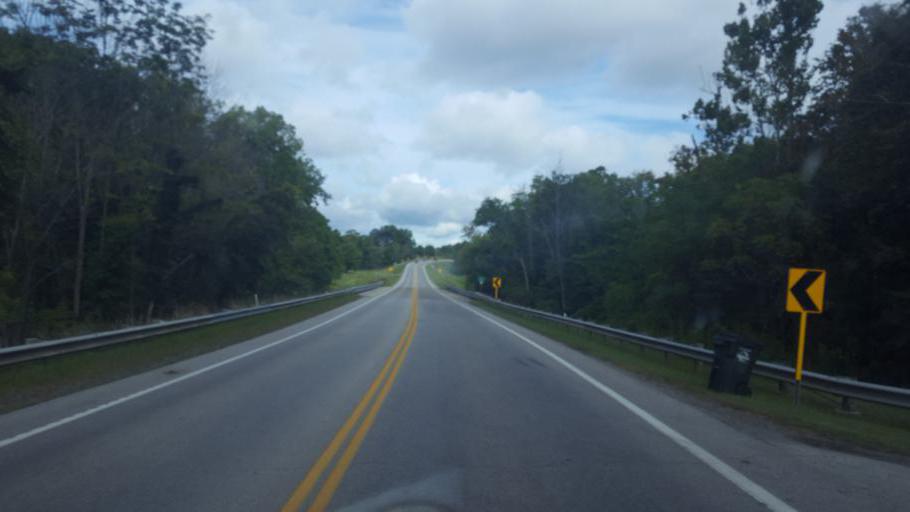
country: US
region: Ohio
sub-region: Lorain County
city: Wellington
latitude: 41.2049
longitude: -82.2166
